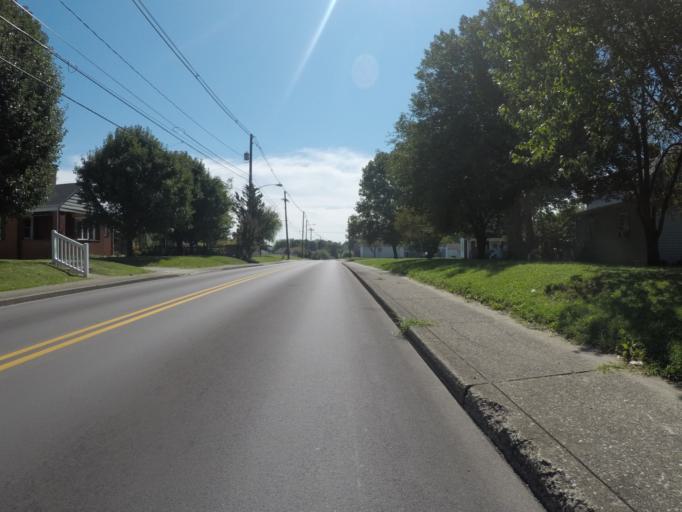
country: US
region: Kentucky
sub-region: Boyd County
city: Ashland
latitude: 38.4556
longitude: -82.6451
